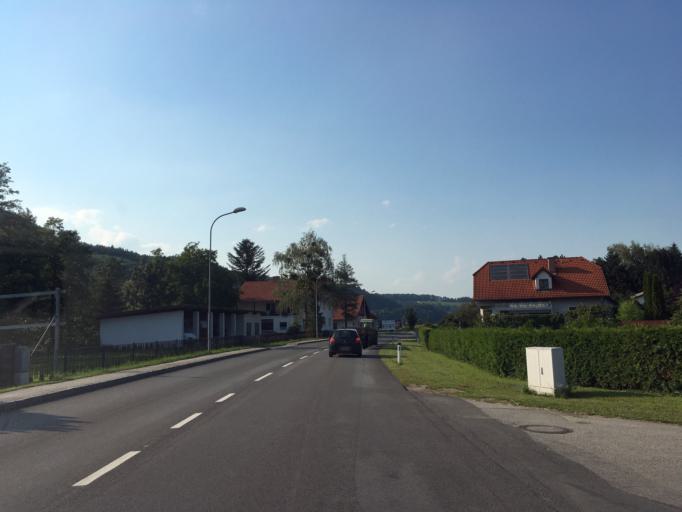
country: AT
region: Lower Austria
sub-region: Politischer Bezirk Neunkirchen
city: Warth
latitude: 47.6372
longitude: 16.1302
